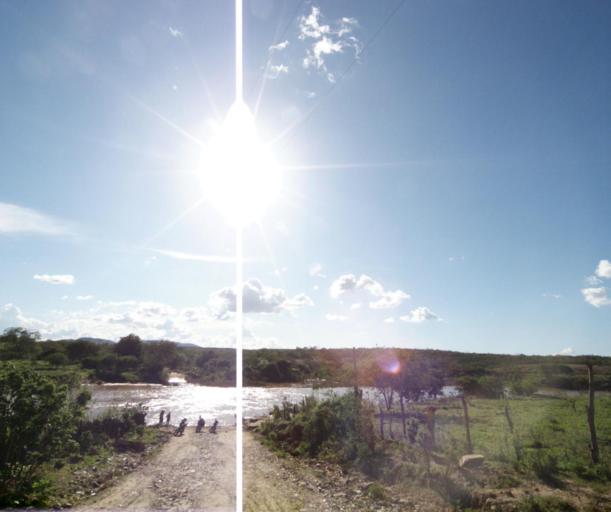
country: BR
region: Bahia
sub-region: Tanhacu
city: Tanhacu
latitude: -14.1827
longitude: -41.0147
